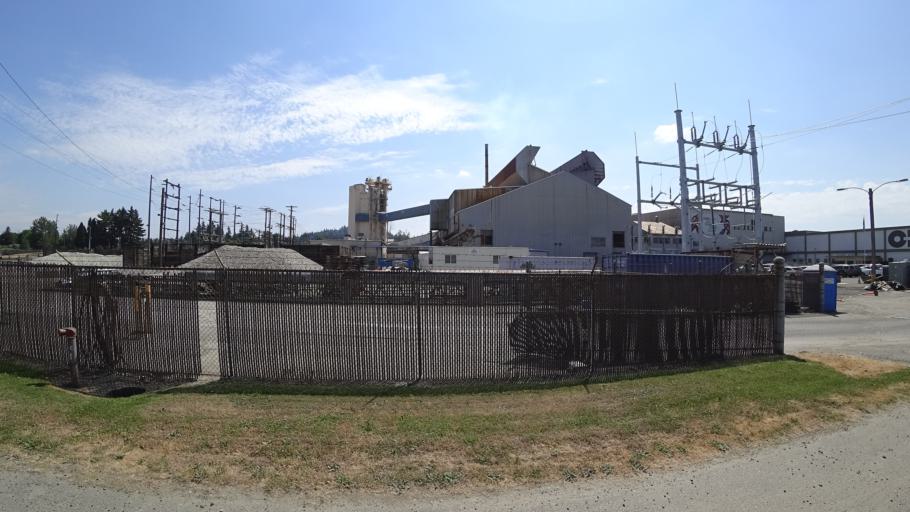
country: US
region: Oregon
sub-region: Multnomah County
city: Lents
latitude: 45.5636
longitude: -122.5631
